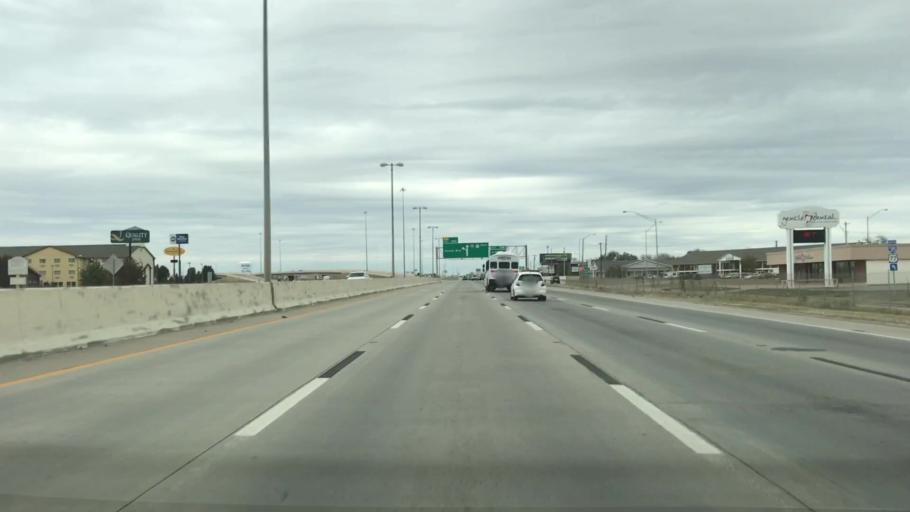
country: US
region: Oklahoma
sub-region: Cleveland County
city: Moore
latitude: 35.3518
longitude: -97.4946
